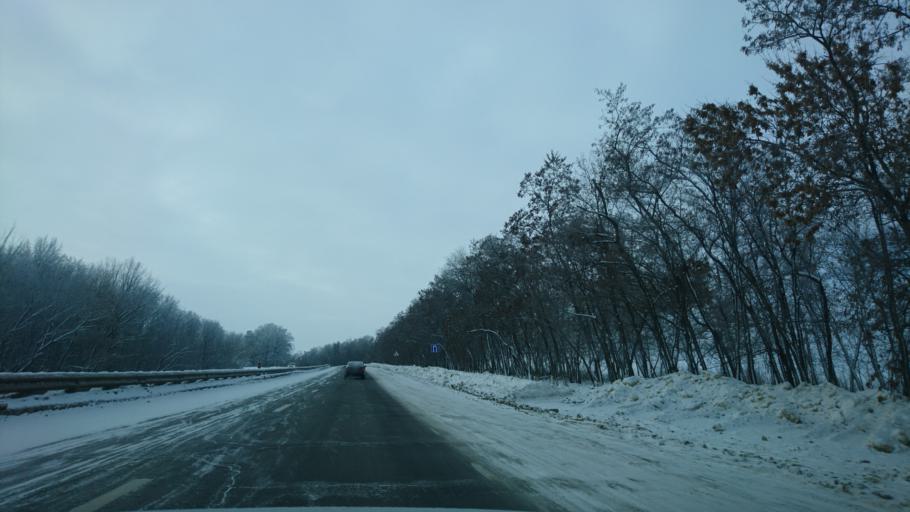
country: RU
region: Belgorod
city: Mayskiy
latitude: 50.4850
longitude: 36.4101
